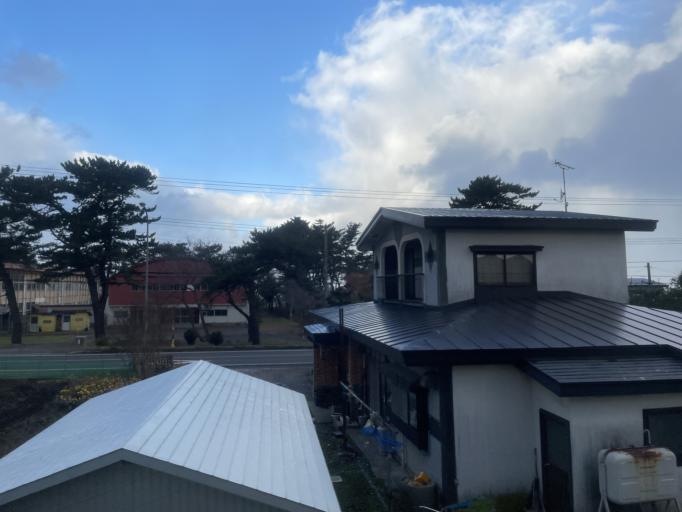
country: JP
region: Aomori
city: Mutsu
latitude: 41.1135
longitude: 141.2561
